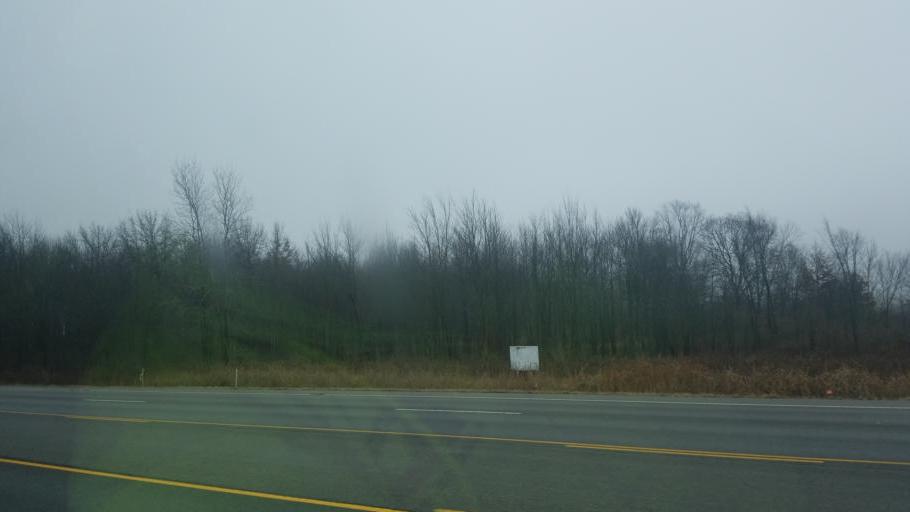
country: US
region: Ohio
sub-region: Champaign County
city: North Lewisburg
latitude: 40.2777
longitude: -83.5284
